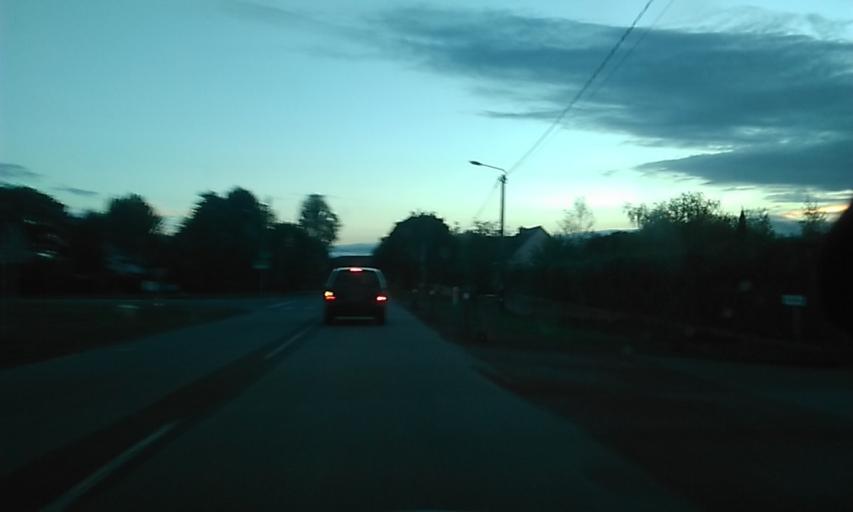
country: FR
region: Brittany
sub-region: Departement d'Ille-et-Vilaine
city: Saint-Thurial
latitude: 48.0479
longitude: -1.9297
